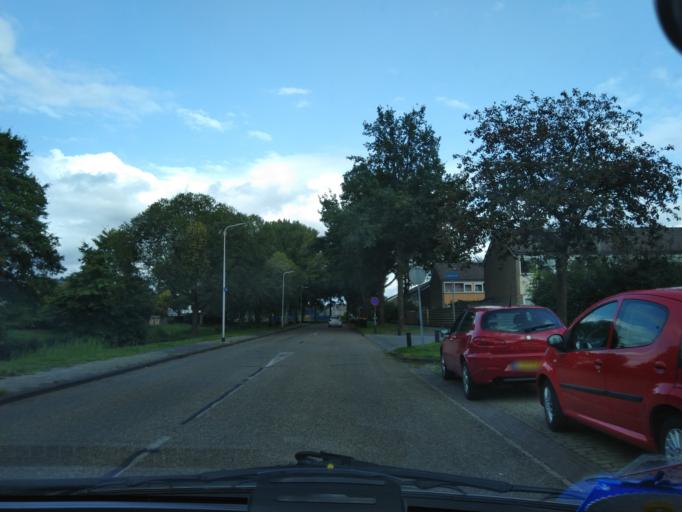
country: NL
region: Drenthe
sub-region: Gemeente Assen
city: Assen
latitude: 53.0048
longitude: 6.5383
